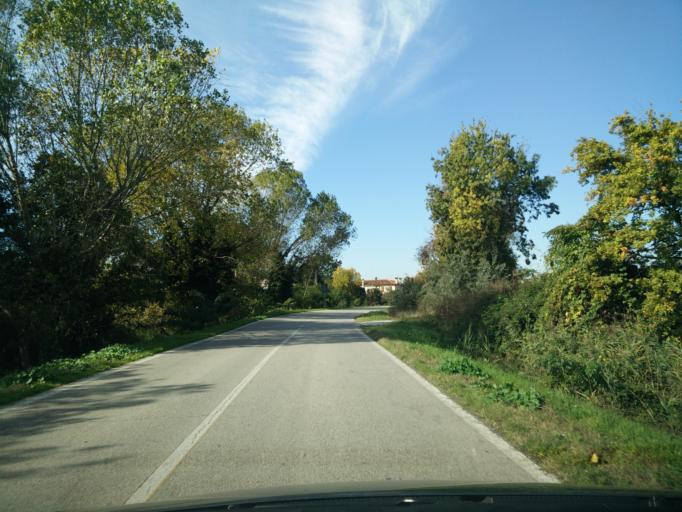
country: IT
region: Veneto
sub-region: Provincia di Venezia
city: Mestre
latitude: 45.4289
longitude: 12.2230
